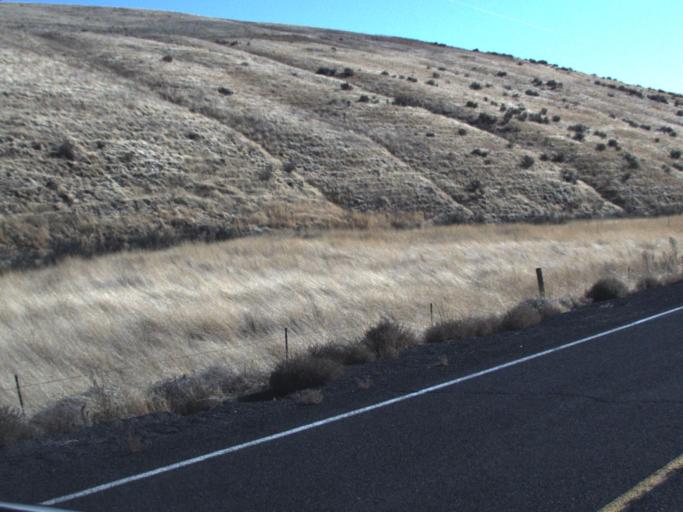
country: US
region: Washington
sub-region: Franklin County
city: Connell
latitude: 46.6705
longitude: -118.5464
